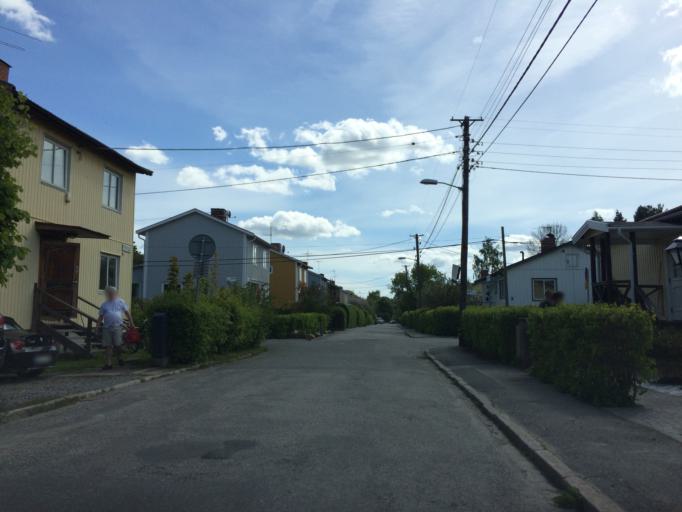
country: SE
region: Stockholm
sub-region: Huddinge Kommun
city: Huddinge
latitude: 59.2821
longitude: 17.9961
